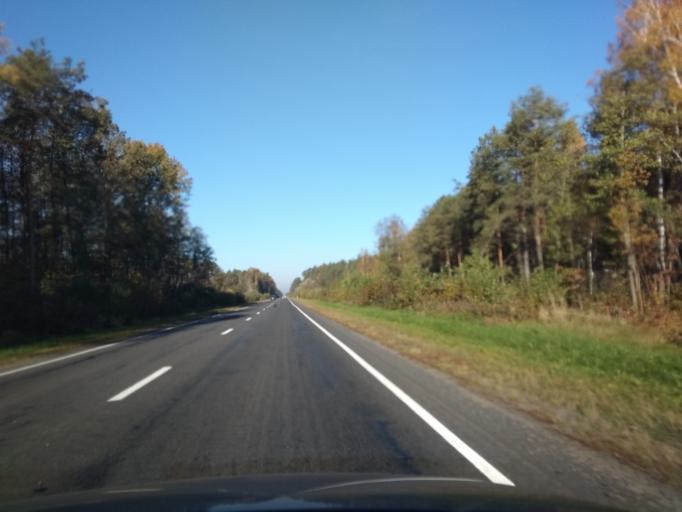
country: BY
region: Brest
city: Malaryta
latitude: 51.9062
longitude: 24.1117
